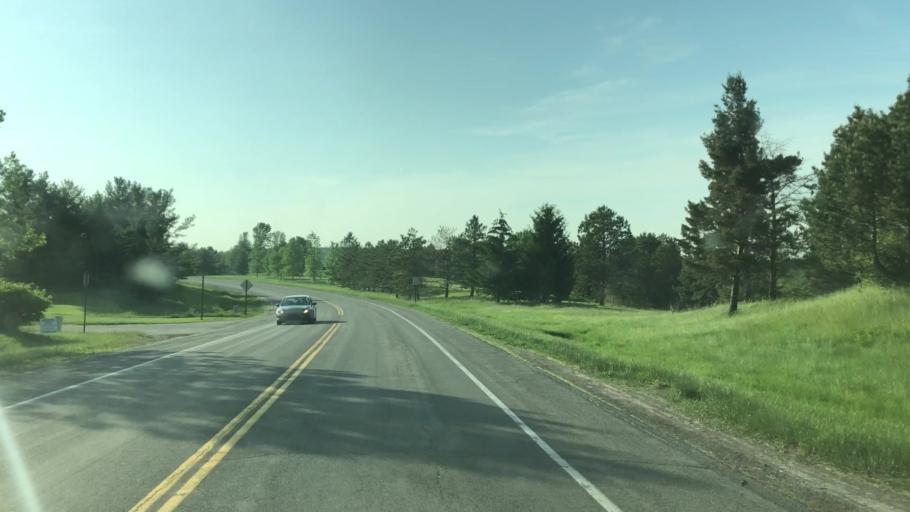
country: US
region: New York
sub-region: Wayne County
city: Macedon
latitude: 43.1209
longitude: -77.3150
